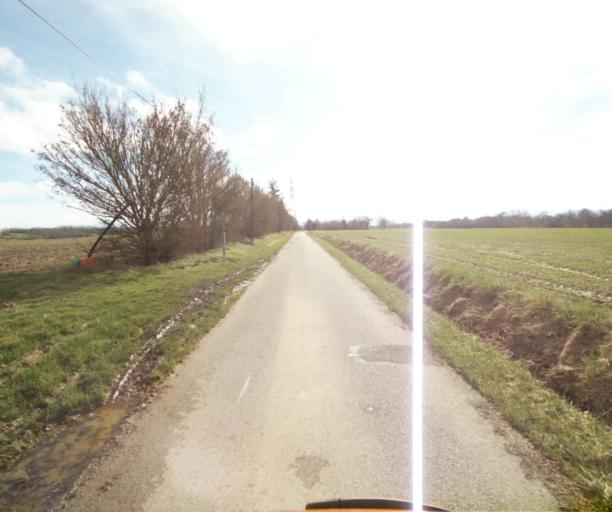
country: FR
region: Midi-Pyrenees
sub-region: Departement de l'Ariege
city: La Tour-du-Crieu
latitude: 43.1268
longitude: 1.6952
